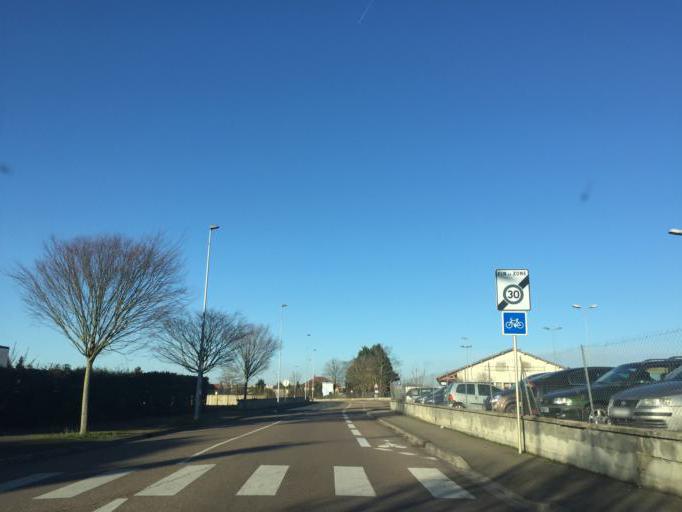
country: FR
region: Bourgogne
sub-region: Departement de l'Yonne
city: Auxerre
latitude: 47.7982
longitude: 3.5847
